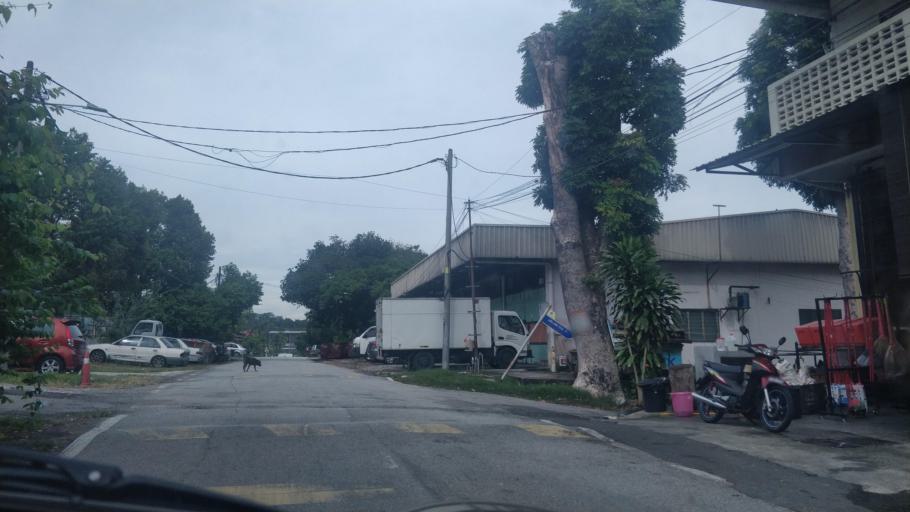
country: MY
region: Selangor
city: Kuang
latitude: 3.2035
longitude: 101.5961
